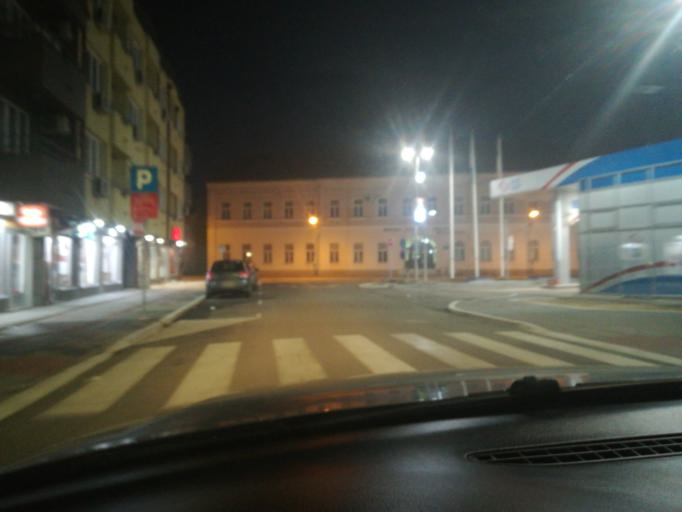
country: RS
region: Central Serbia
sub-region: Branicevski Okrug
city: Pozarevac
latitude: 44.6221
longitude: 21.1832
